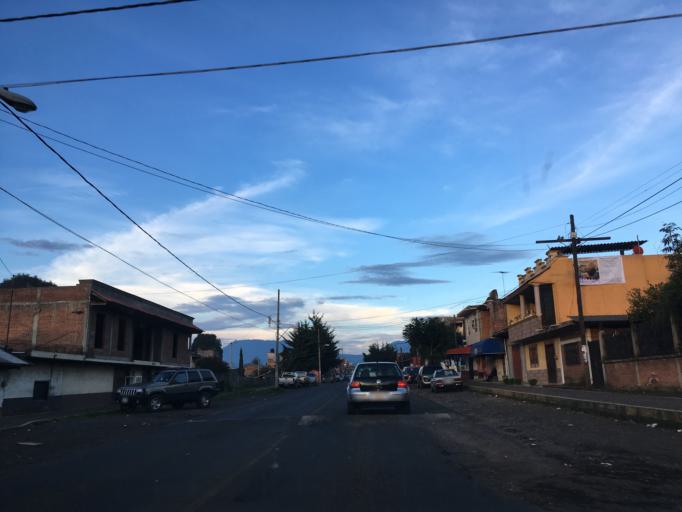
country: MX
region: Michoacan
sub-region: Salvador Escalante
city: Santa Clara del Cobre
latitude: 19.4034
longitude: -101.6463
